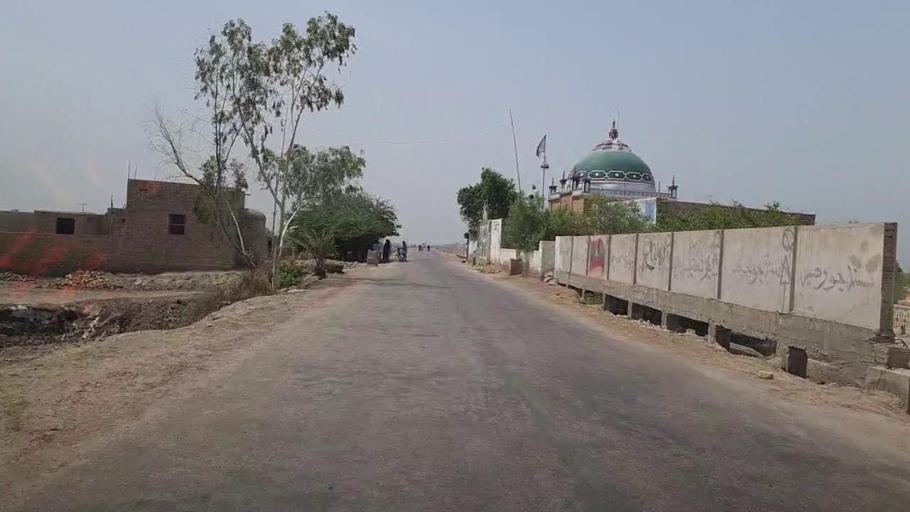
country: PK
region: Sindh
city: Radhan
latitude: 27.1618
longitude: 67.9430
